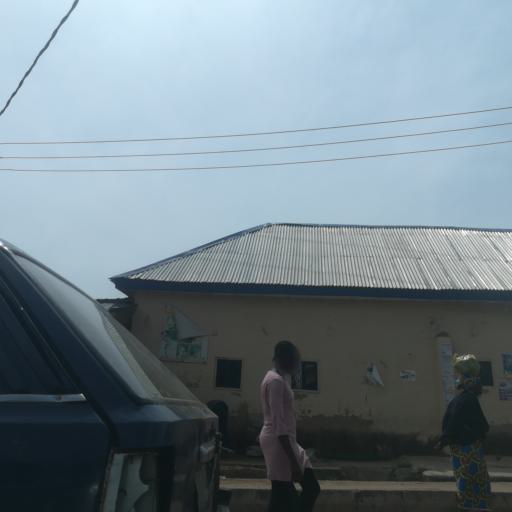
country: NG
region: Plateau
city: Jos
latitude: 9.9288
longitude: 8.8675
